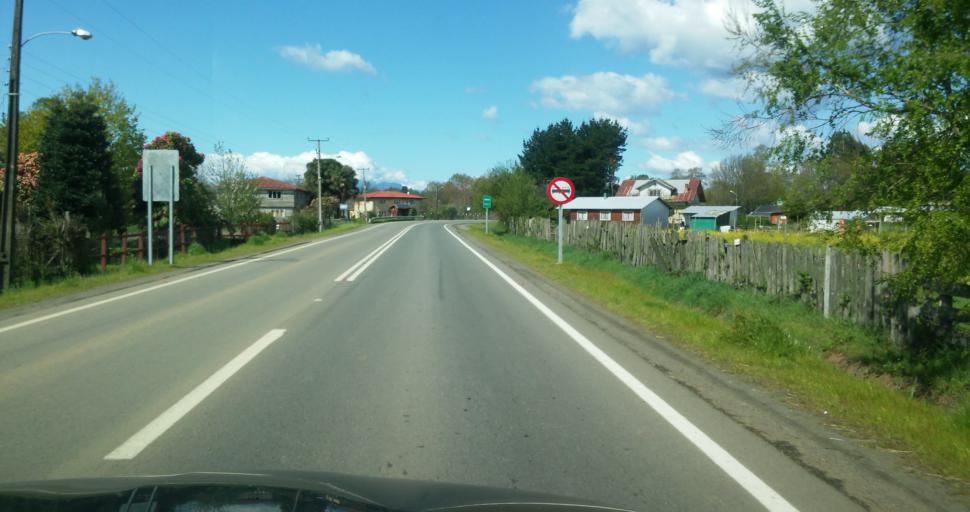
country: CL
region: Los Rios
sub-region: Provincia del Ranco
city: Rio Bueno
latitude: -40.2392
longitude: -72.5946
